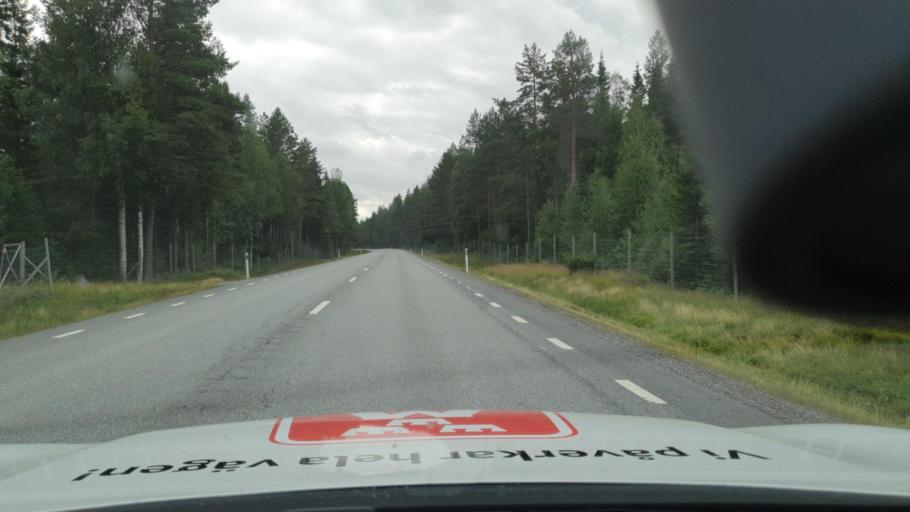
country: SE
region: Vaesterbotten
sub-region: Skelleftea Kommun
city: Burea
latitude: 64.5310
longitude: 21.2582
